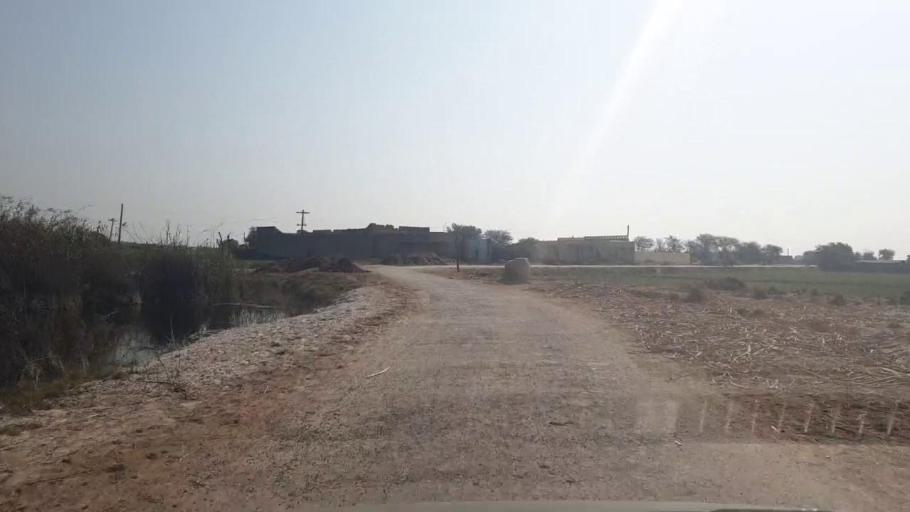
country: PK
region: Sindh
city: Tando Adam
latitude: 25.7453
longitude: 68.6159
